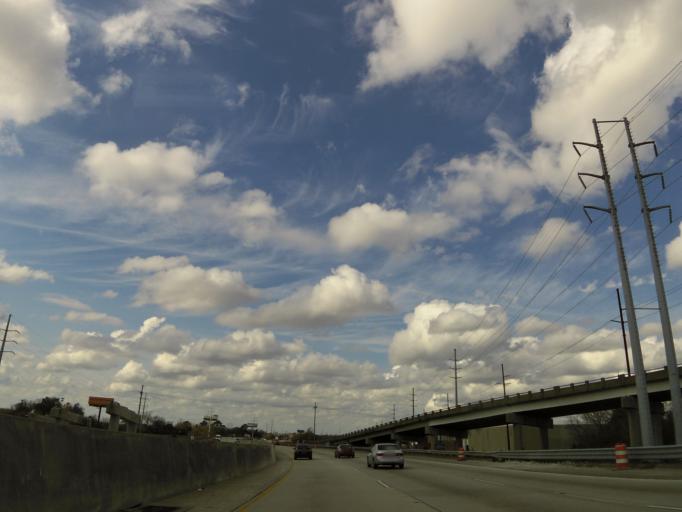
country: US
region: South Carolina
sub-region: Charleston County
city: North Charleston
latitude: 32.8366
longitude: -79.9617
